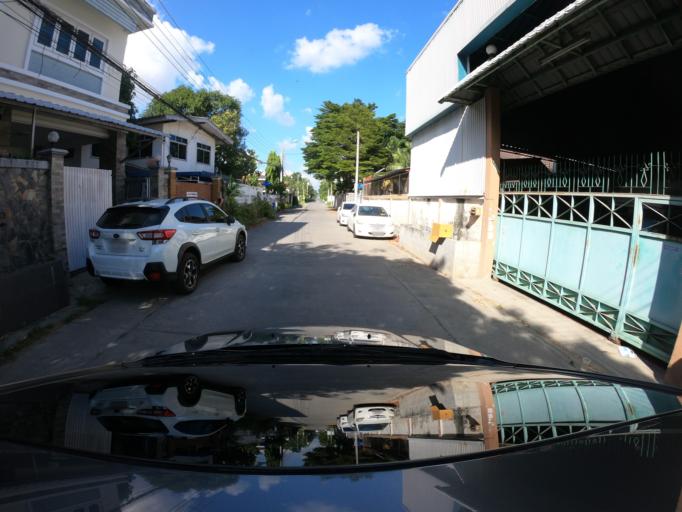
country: TH
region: Bangkok
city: Bang Na
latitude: 13.6507
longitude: 100.6233
